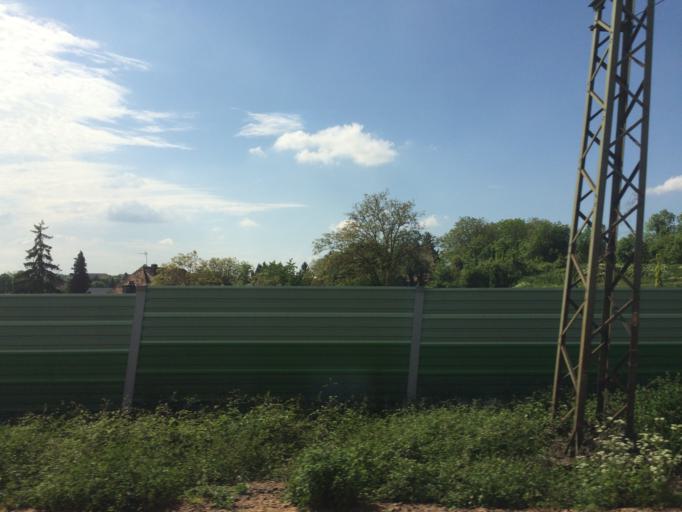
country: DE
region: Bavaria
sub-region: Regierungsbezirk Unterfranken
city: Kitzingen
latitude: 49.7384
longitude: 10.1551
